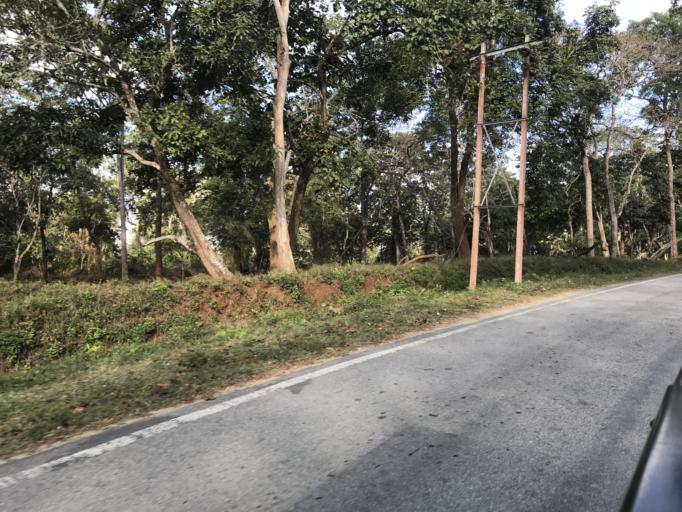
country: IN
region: Karnataka
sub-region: Mysore
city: Heggadadevankote
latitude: 11.9483
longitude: 76.2291
